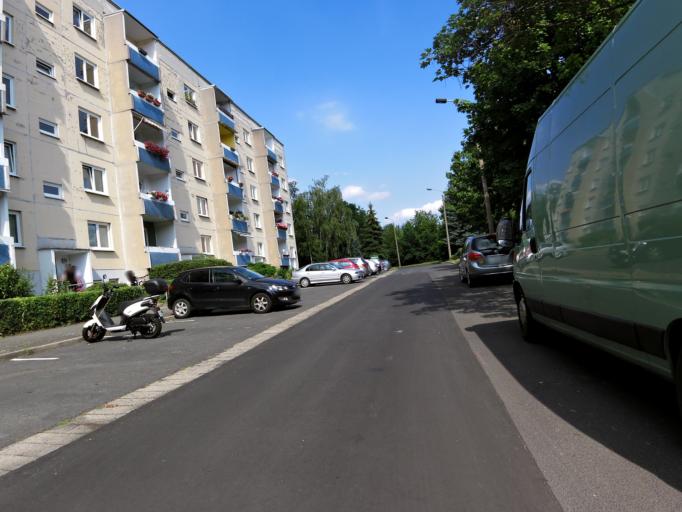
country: DE
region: Saxony
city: Leipzig
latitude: 51.3533
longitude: 12.4275
